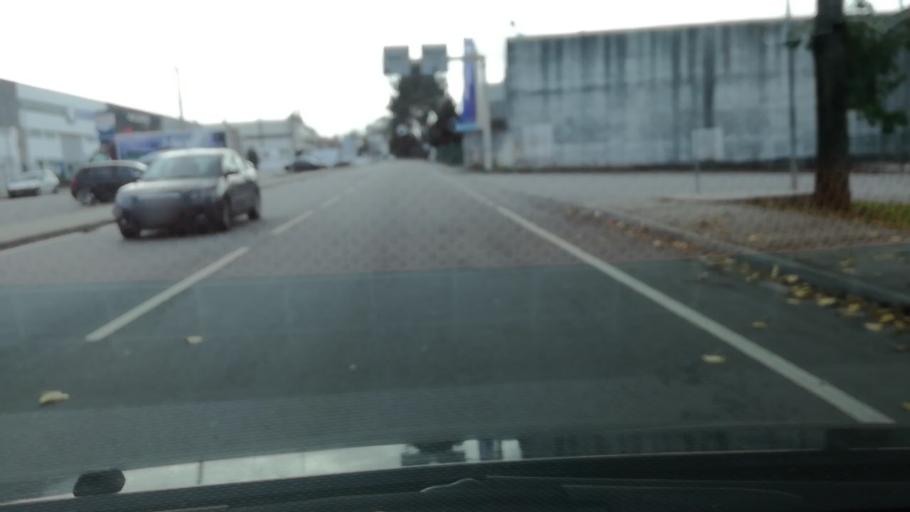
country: PT
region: Porto
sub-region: Maia
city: Gemunde
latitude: 41.2624
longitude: -8.6472
